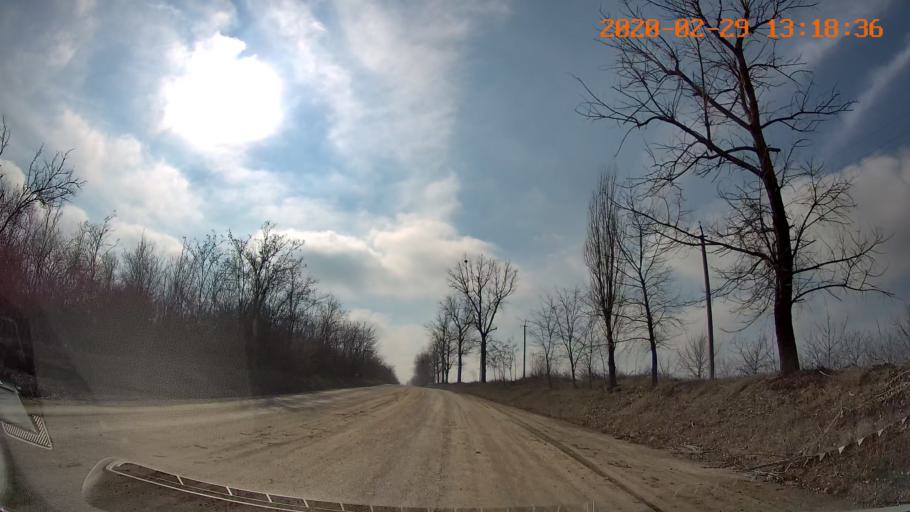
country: MD
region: Telenesti
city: Camenca
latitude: 47.9931
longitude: 28.6563
